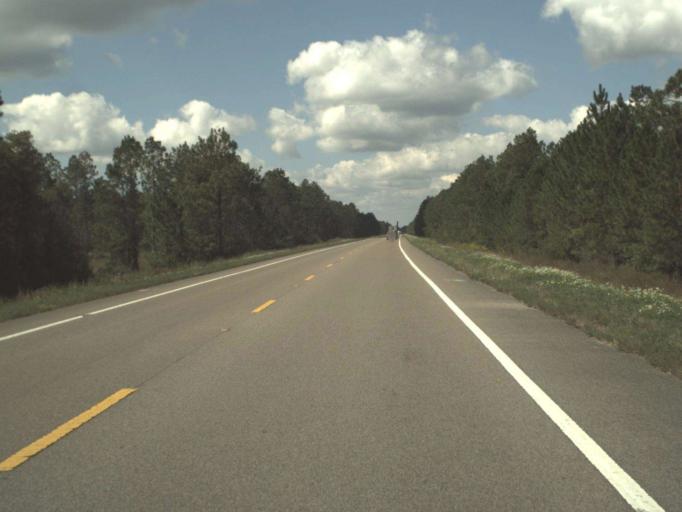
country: US
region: Florida
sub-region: Bay County
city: Laguna Beach
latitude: 30.4532
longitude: -85.9047
